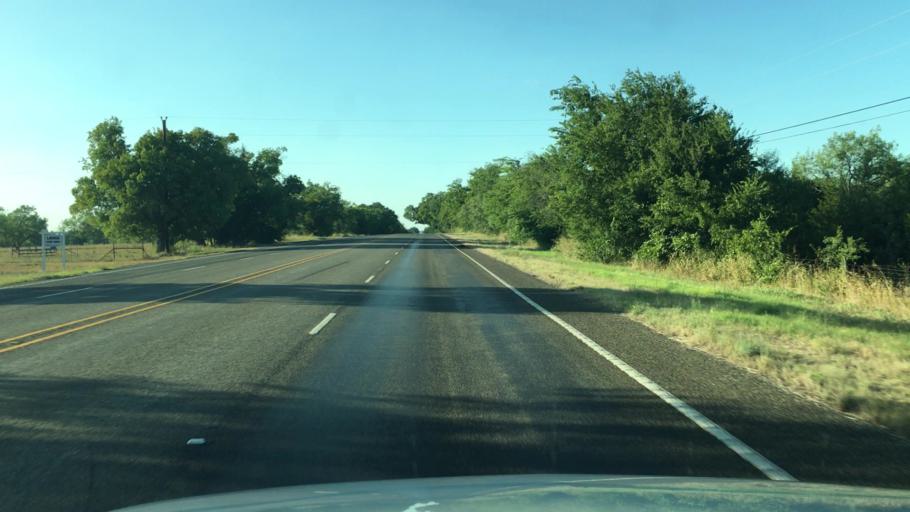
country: US
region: Texas
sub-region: Lampasas County
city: Lampasas
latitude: 31.3345
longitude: -98.1739
